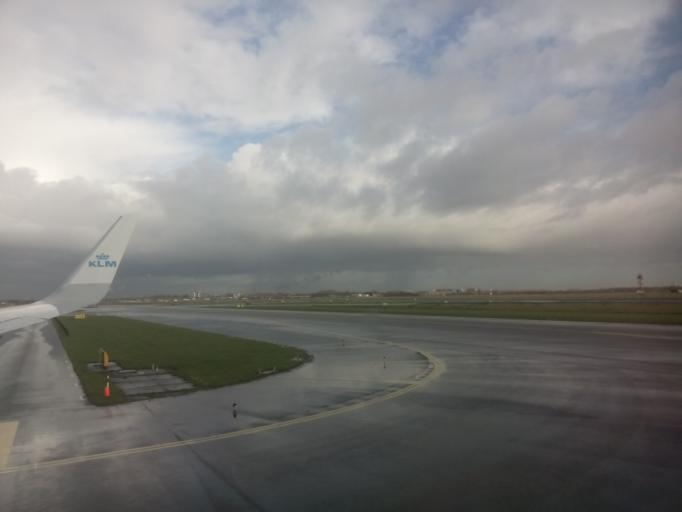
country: NL
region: North Holland
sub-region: Gemeente Aalsmeer
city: Aalsmeer
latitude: 52.3084
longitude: 4.7755
